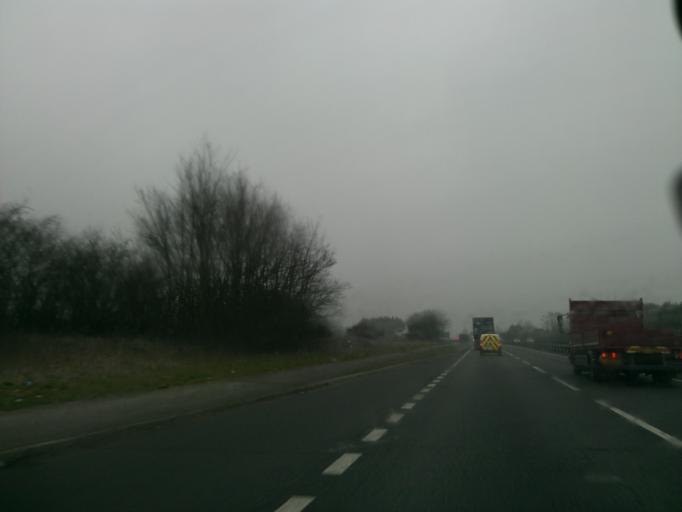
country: GB
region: England
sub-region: Essex
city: Marks Tey
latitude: 51.8690
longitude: 0.7657
